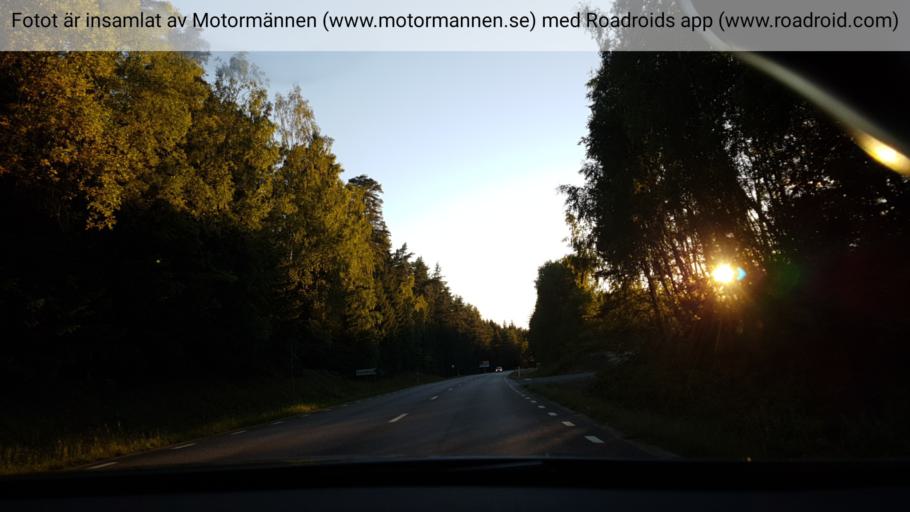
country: SE
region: Vaestra Goetaland
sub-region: Tibro Kommun
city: Tibro
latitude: 58.3428
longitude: 14.1595
